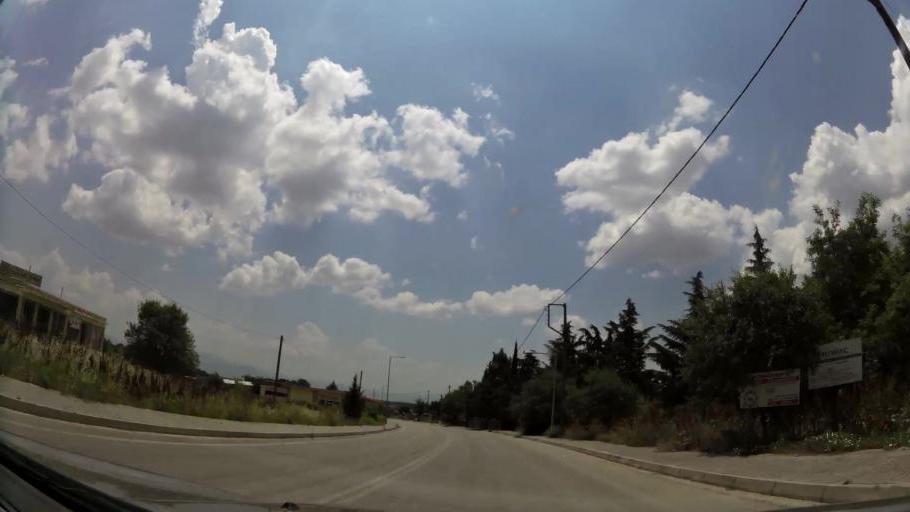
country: GR
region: West Macedonia
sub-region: Nomos Kozanis
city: Kozani
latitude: 40.2886
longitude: 21.7983
